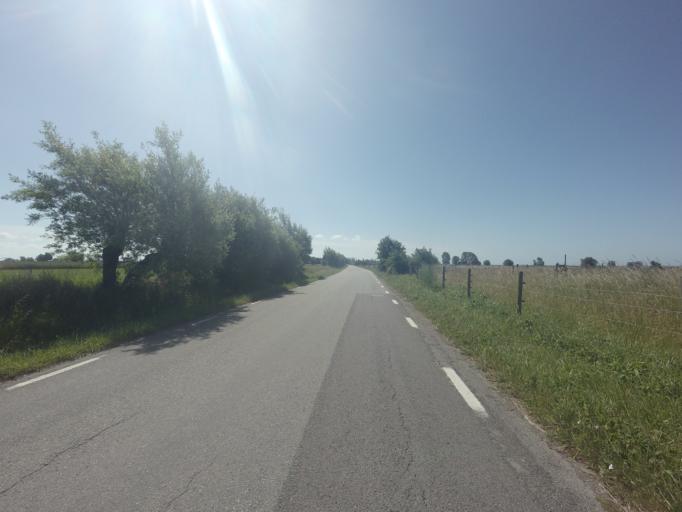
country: SE
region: Skane
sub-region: Malmo
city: Bunkeflostrand
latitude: 55.5082
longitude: 12.9392
